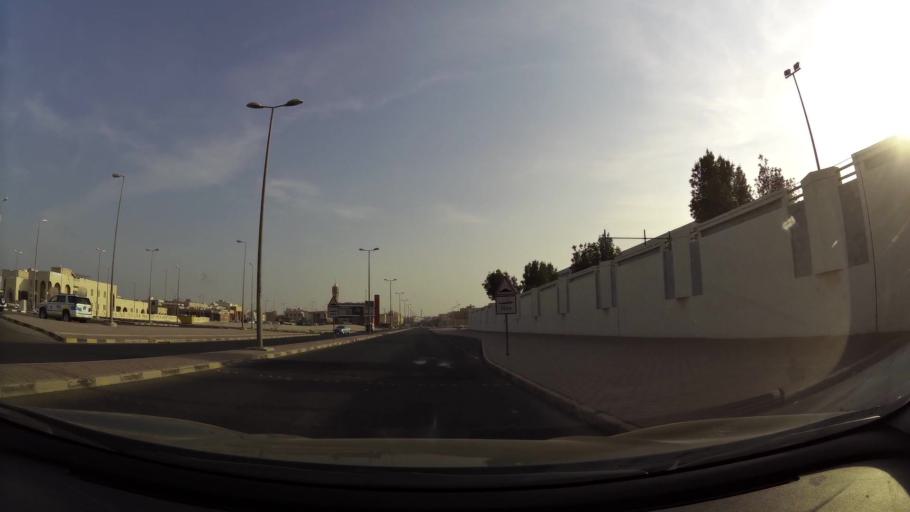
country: KW
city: Al Funaytis
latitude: 29.2375
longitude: 48.0777
